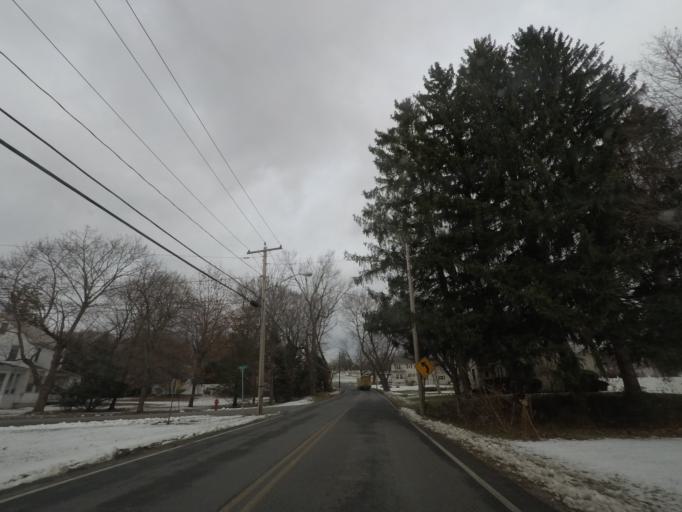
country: US
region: New York
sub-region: Rensselaer County
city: East Greenbush
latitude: 42.5872
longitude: -73.7049
